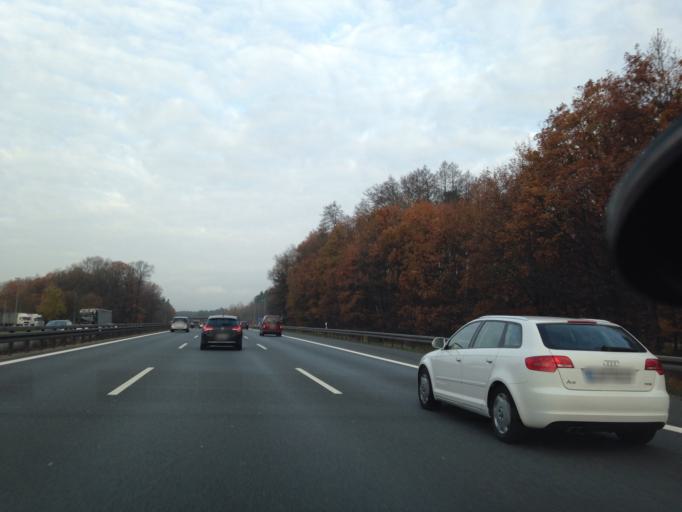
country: DE
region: Bavaria
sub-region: Regierungsbezirk Mittelfranken
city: Wetzendorf
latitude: 49.5251
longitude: 11.0695
